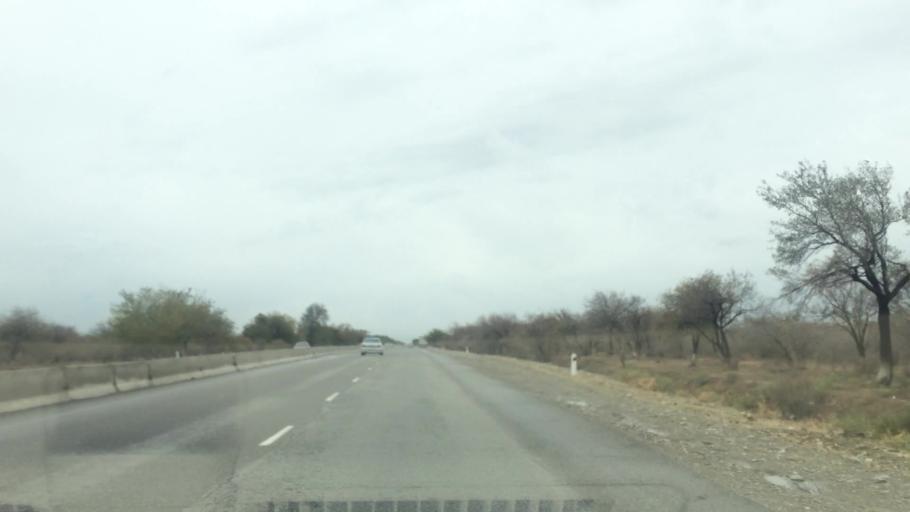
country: UZ
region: Samarqand
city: Bulung'ur
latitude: 39.8188
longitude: 67.3849
